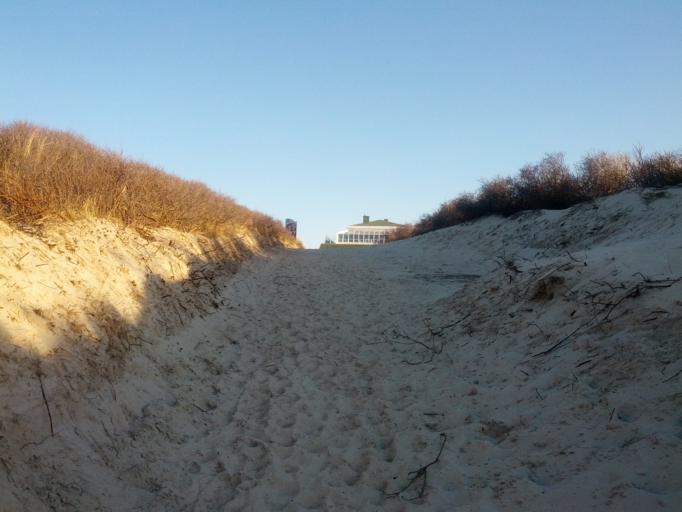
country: DE
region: Lower Saxony
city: Langeoog
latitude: 53.7536
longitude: 7.4809
